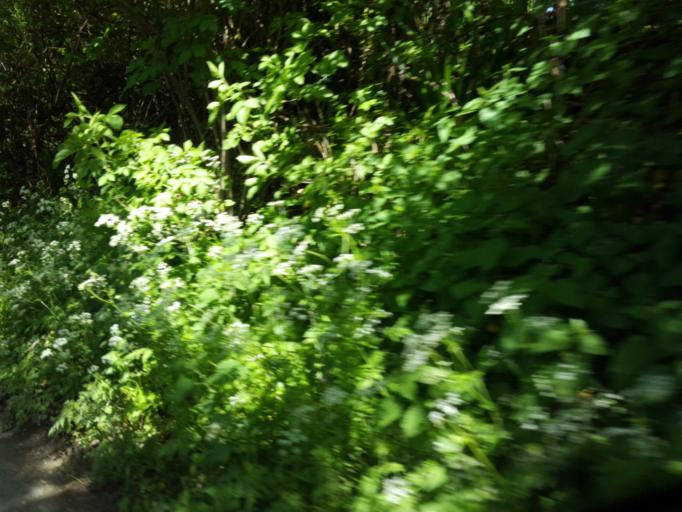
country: GB
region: England
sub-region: Gloucestershire
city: Stroud
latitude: 51.7570
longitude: -2.1849
